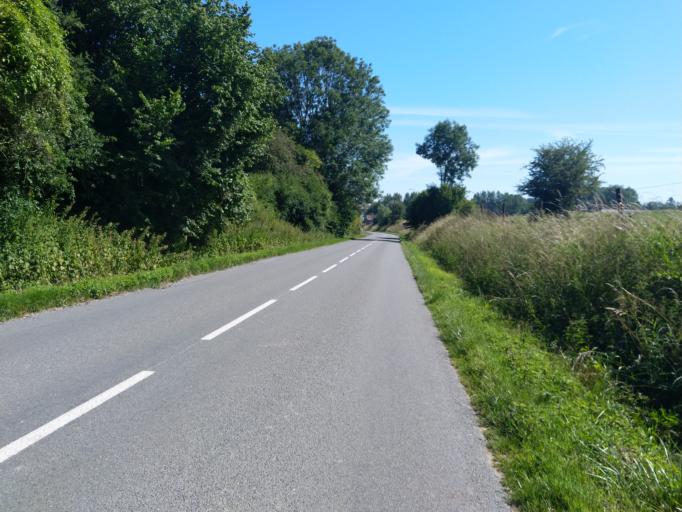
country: FR
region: Nord-Pas-de-Calais
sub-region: Departement du Nord
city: Bavay
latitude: 50.3220
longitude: 3.8227
